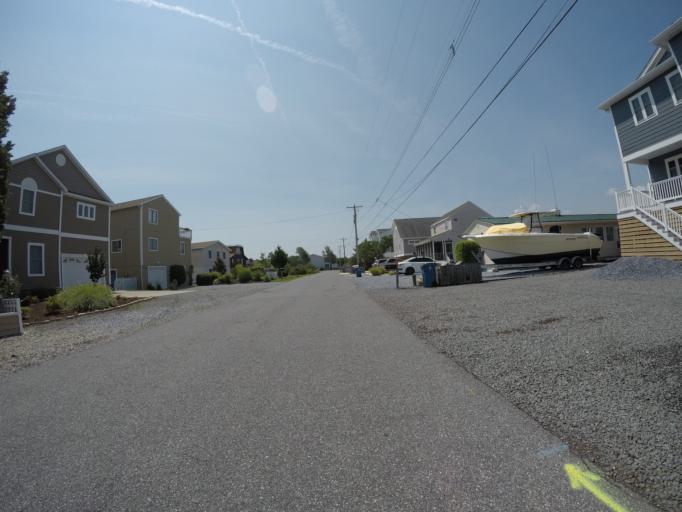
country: US
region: Delaware
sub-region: Sussex County
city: Bethany Beach
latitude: 38.5122
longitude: -75.0563
